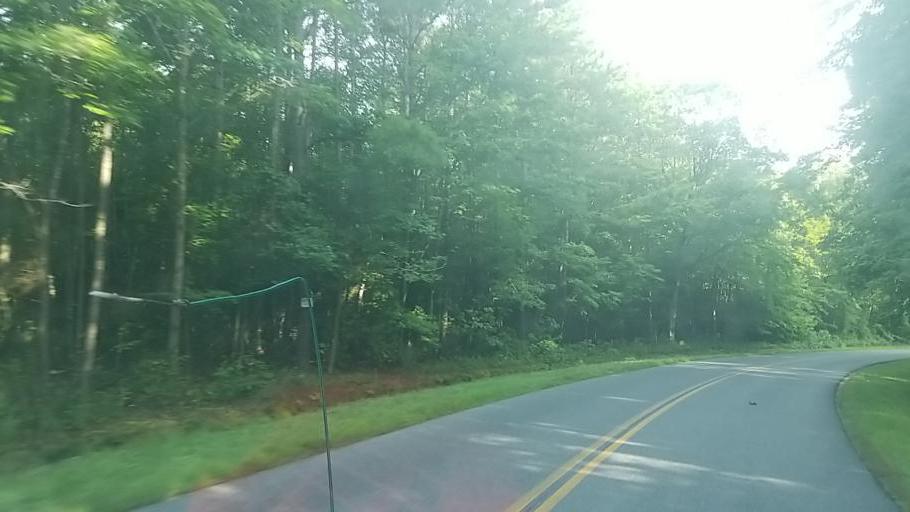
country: US
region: Maryland
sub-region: Worcester County
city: West Ocean City
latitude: 38.3195
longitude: -75.1468
